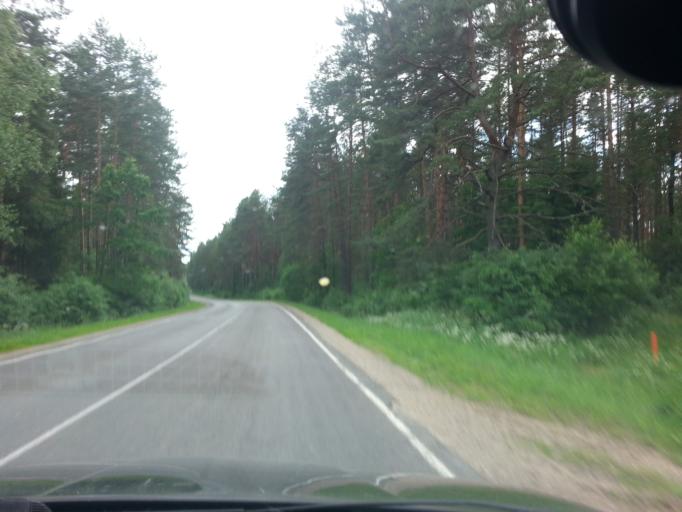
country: BY
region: Minsk
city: Svir
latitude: 54.8231
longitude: 26.1844
